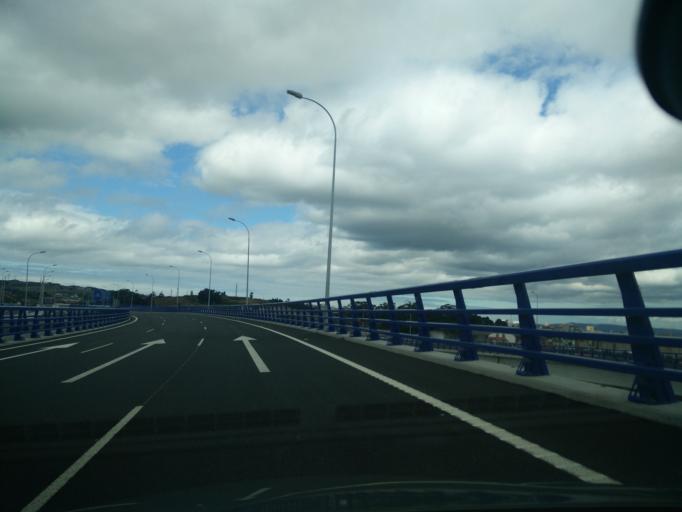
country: ES
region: Galicia
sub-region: Provincia da Coruna
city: A Coruna
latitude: 43.3350
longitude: -8.4211
